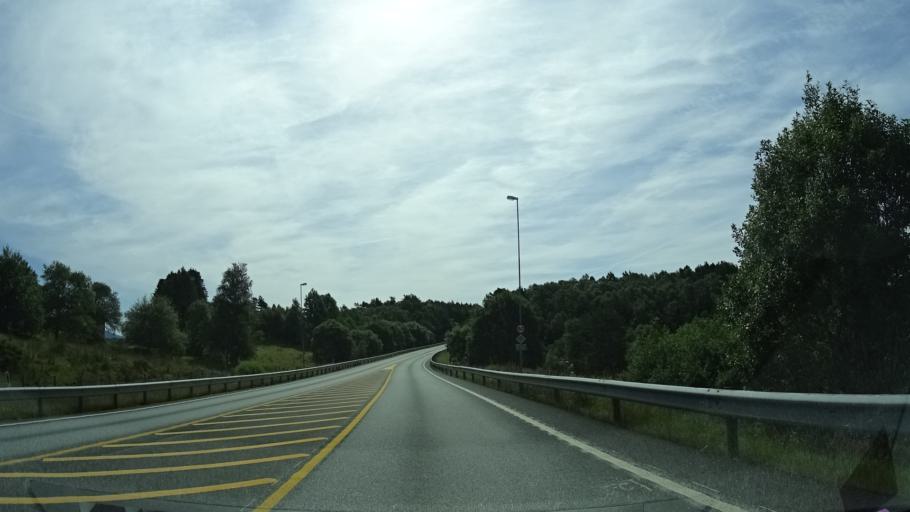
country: NO
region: Hordaland
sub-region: Sveio
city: Sveio
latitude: 59.5607
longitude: 5.4166
